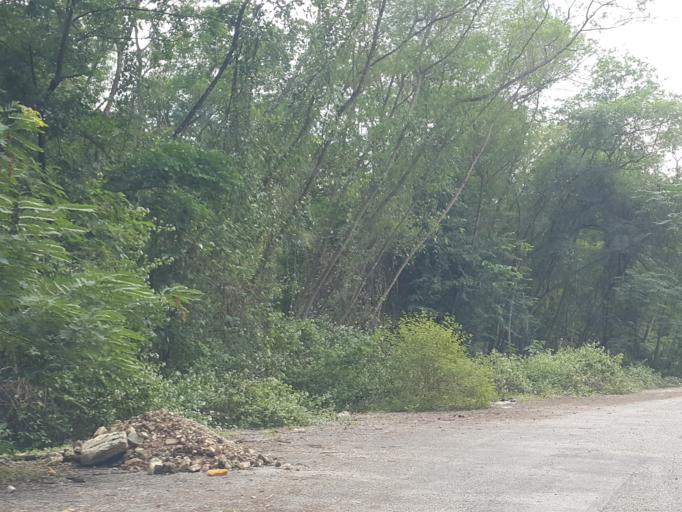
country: TH
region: Lampang
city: Mae Mo
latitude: 18.3267
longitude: 99.7530
